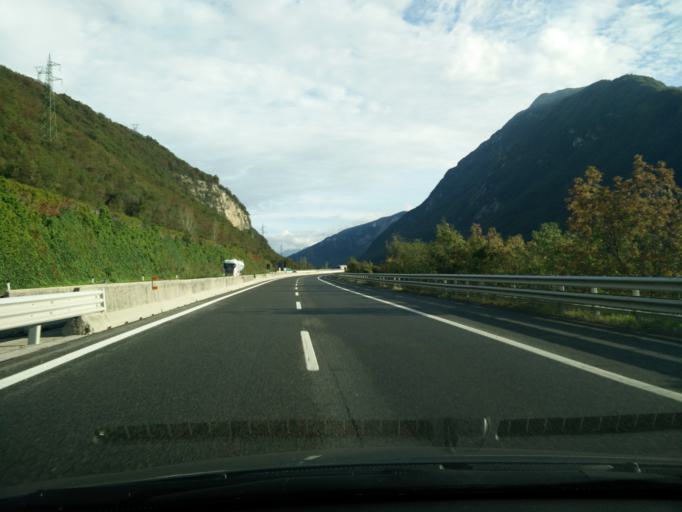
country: IT
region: Veneto
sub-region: Provincia di Treviso
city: Revine
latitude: 46.0243
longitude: 12.2934
